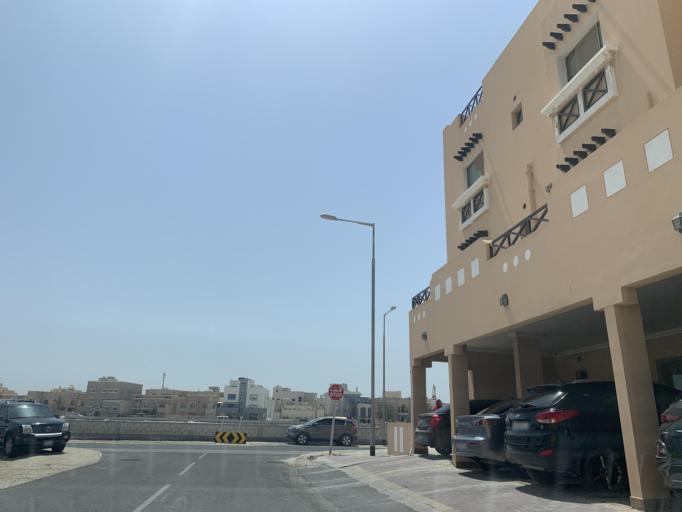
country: BH
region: Muharraq
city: Al Muharraq
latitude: 26.2801
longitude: 50.6050
